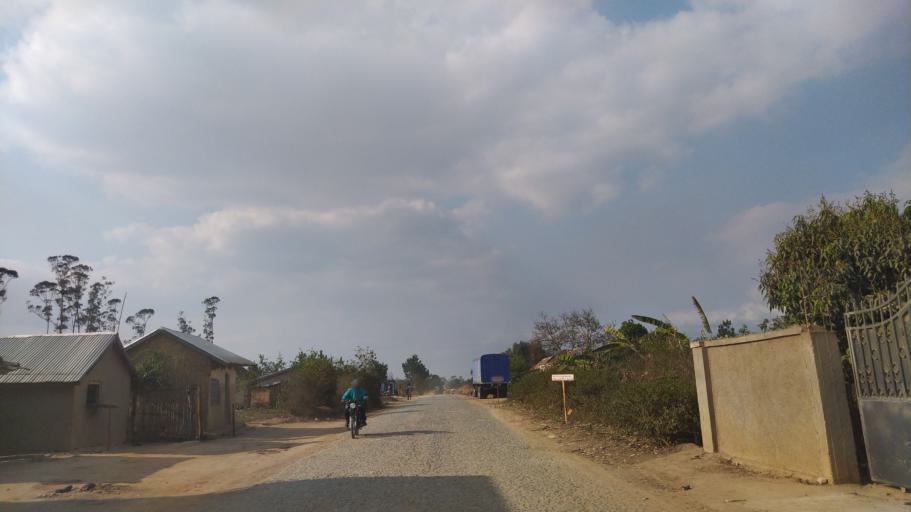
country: MG
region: Alaotra Mangoro
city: Moramanga
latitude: -18.6353
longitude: 48.2758
